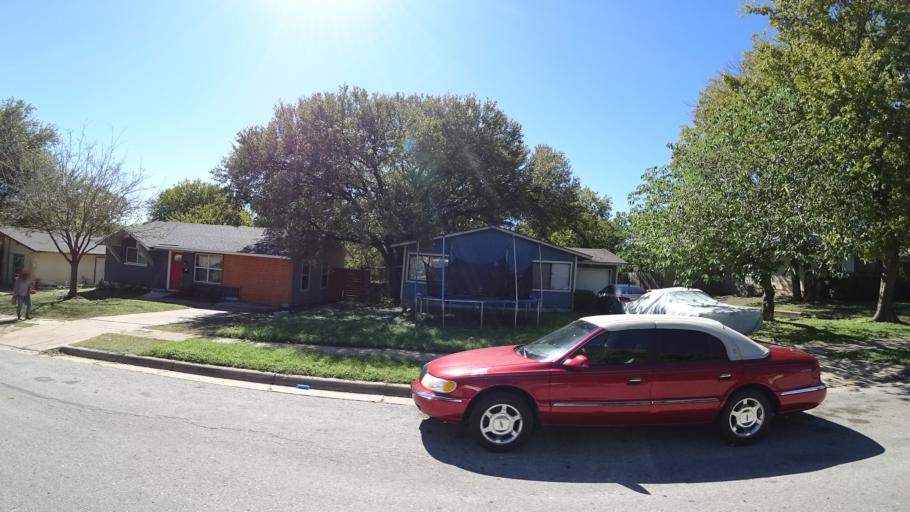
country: US
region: Texas
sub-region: Travis County
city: Austin
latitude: 30.2822
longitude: -97.6617
